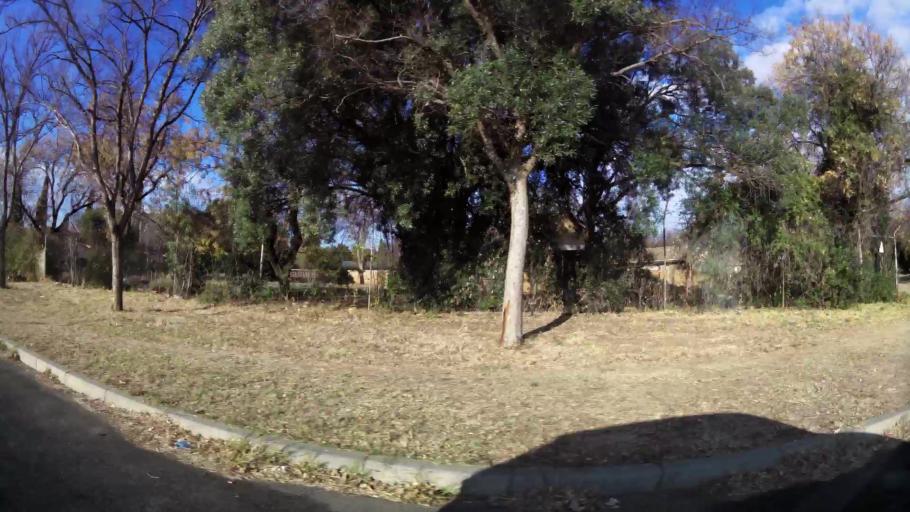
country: ZA
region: Orange Free State
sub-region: Lejweleputswa District Municipality
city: Welkom
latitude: -27.9857
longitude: 26.7265
